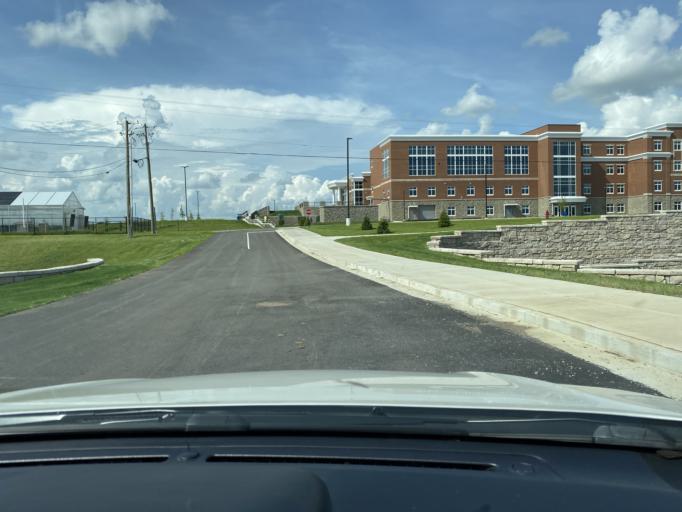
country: US
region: Kentucky
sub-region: Scott County
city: Georgetown
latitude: 38.2148
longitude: -84.6010
